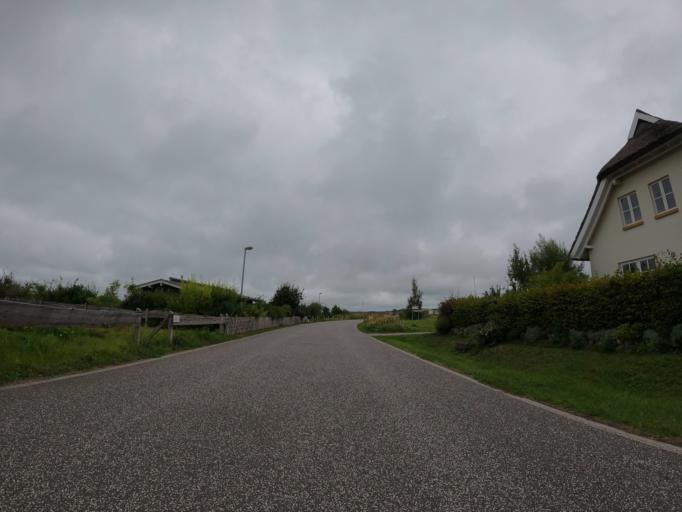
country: DE
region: Mecklenburg-Vorpommern
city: Ostseebad Gohren
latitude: 54.3097
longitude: 13.6808
